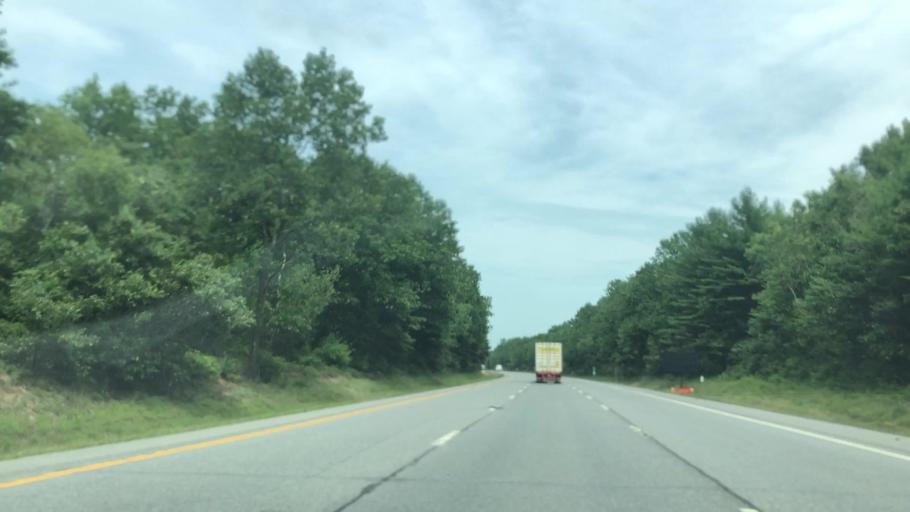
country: US
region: New York
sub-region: Warren County
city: West Glens Falls
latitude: 43.2514
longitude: -73.6836
